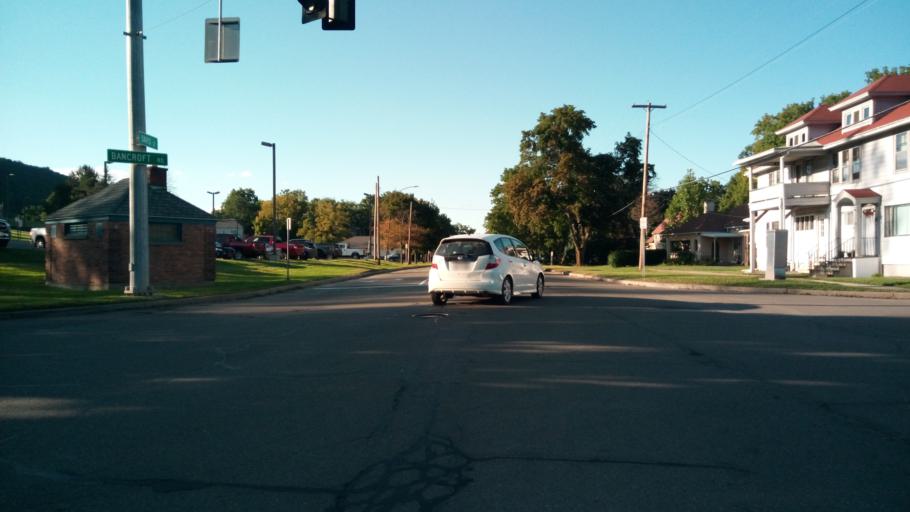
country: US
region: New York
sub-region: Chemung County
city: Elmira Heights
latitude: 42.1143
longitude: -76.8269
